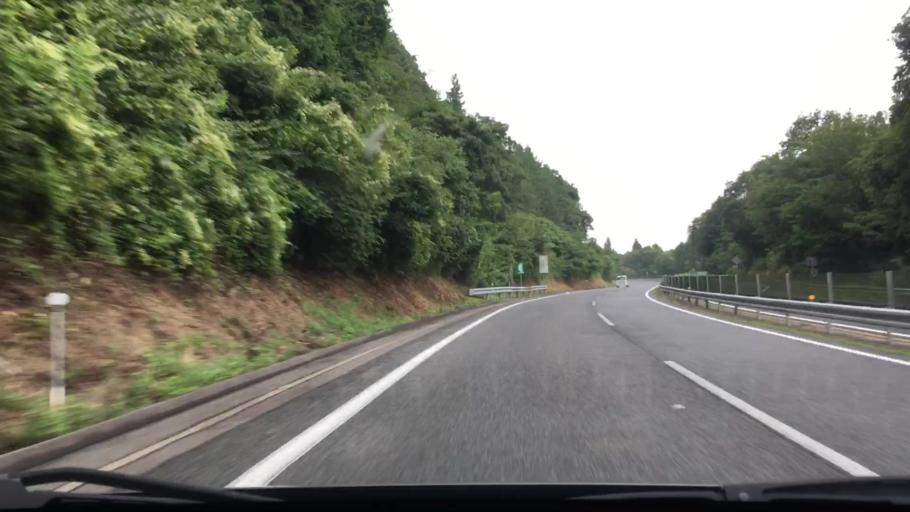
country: JP
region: Hiroshima
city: Miyoshi
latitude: 34.7002
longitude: 132.6070
